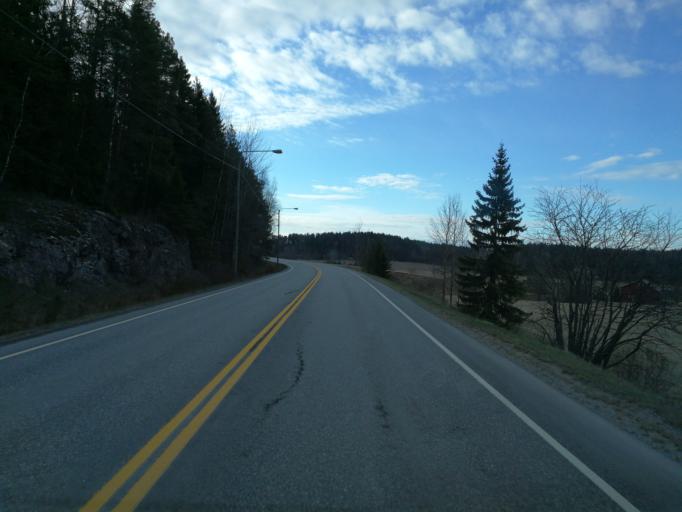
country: FI
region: Varsinais-Suomi
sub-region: Turku
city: Paimio
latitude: 60.4297
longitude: 22.6141
